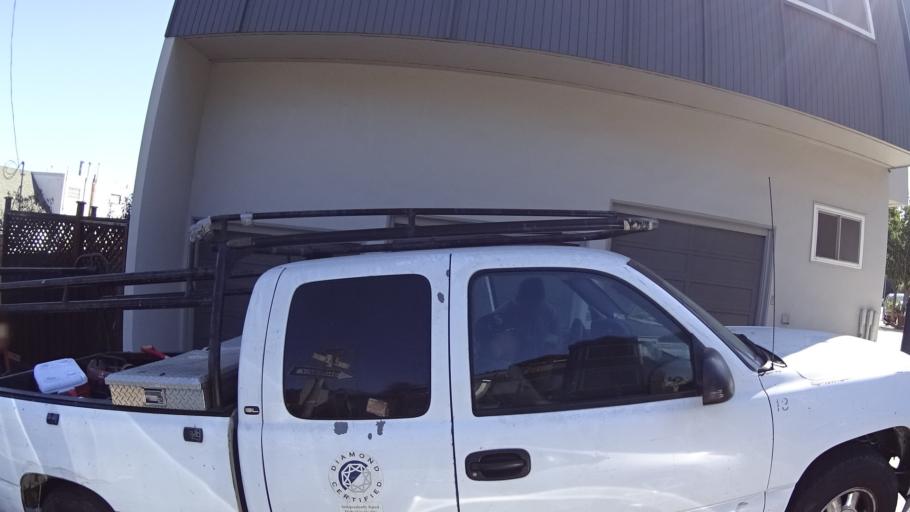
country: US
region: California
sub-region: San Francisco County
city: San Francisco
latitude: 37.7405
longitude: -122.4308
